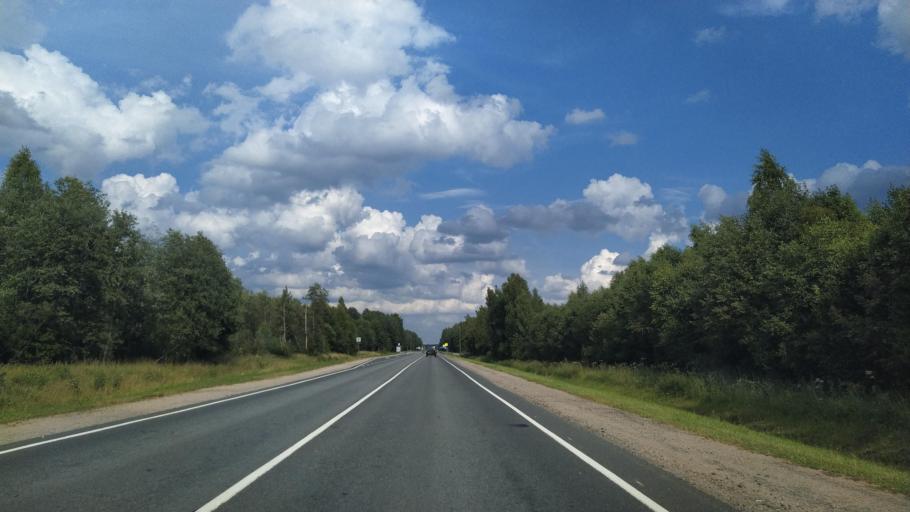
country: RU
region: Novgorod
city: Sol'tsy
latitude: 58.1697
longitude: 30.4886
